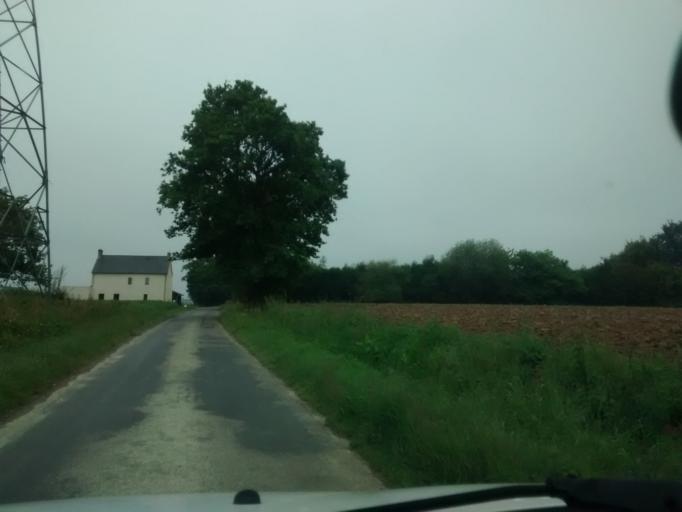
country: FR
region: Brittany
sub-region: Departement d'Ille-et-Vilaine
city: Montgermont
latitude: 48.1430
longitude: -1.7082
